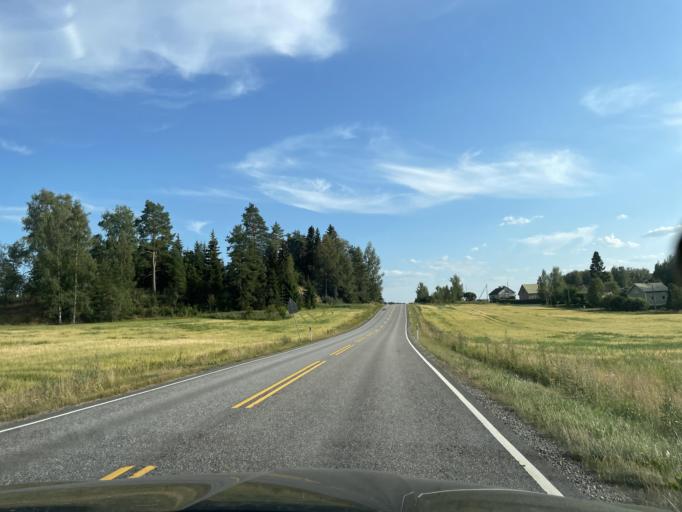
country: FI
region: Paijanne Tavastia
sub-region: Lahti
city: Auttoinen
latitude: 61.2995
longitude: 25.0885
